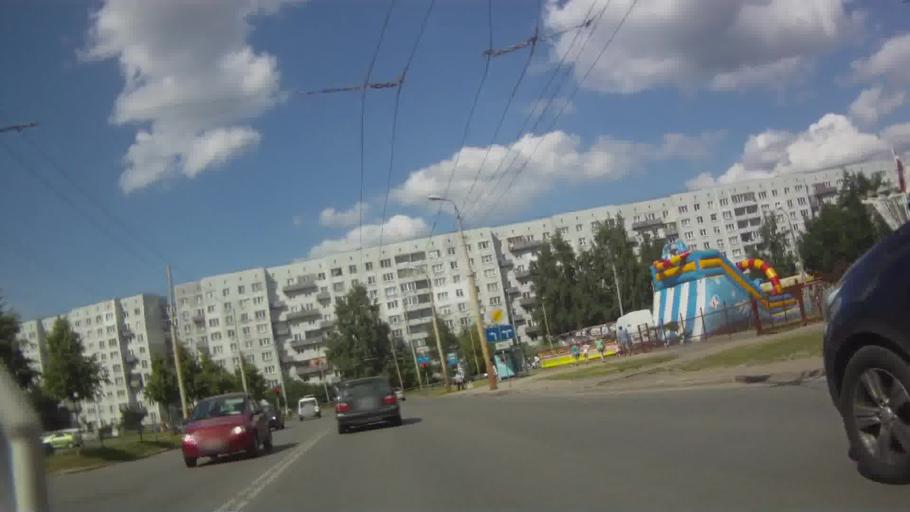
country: LV
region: Riga
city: Riga
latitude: 56.9586
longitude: 24.1772
